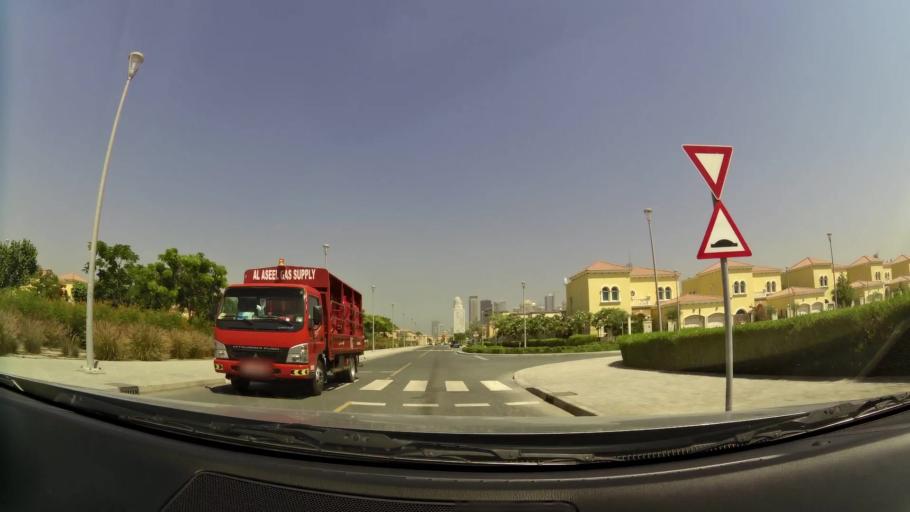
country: AE
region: Dubai
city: Dubai
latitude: 25.0525
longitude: 55.1493
